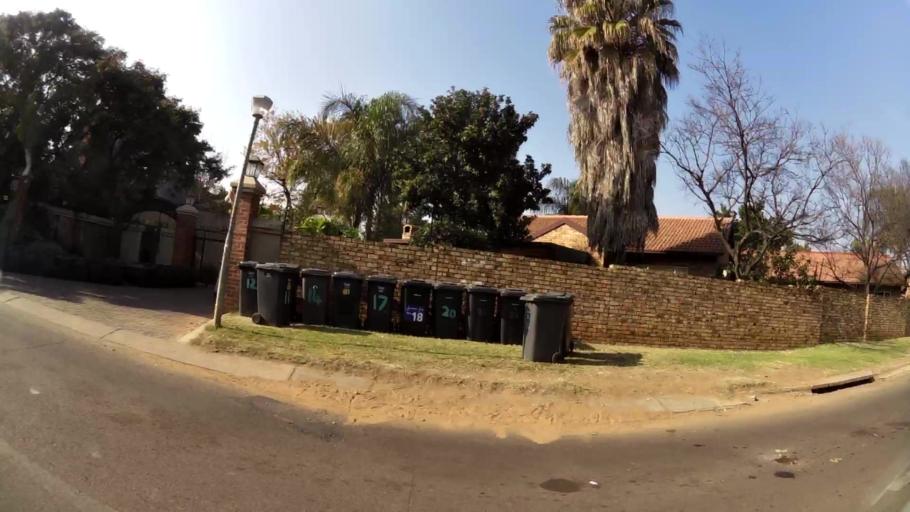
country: ZA
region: Gauteng
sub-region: City of Tshwane Metropolitan Municipality
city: Pretoria
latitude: -25.7670
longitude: 28.3400
